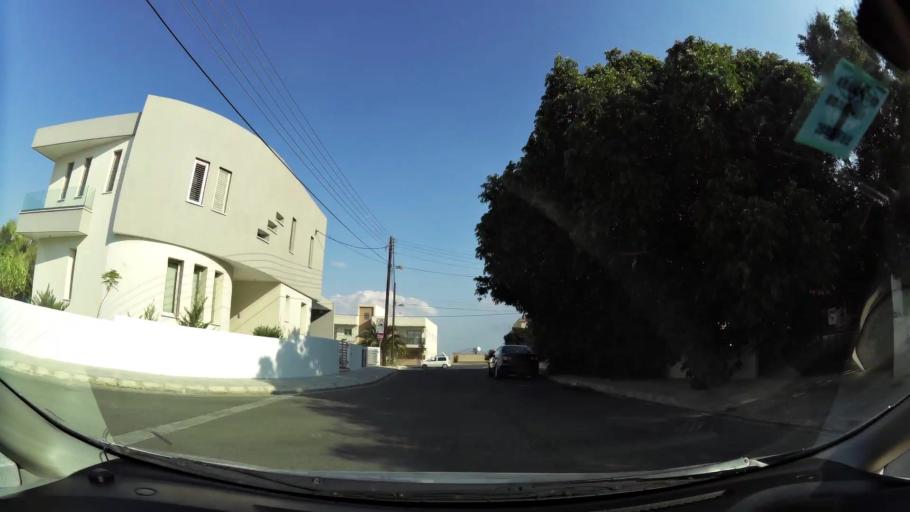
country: CY
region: Lefkosia
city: Kato Deftera
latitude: 35.1221
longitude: 33.2942
